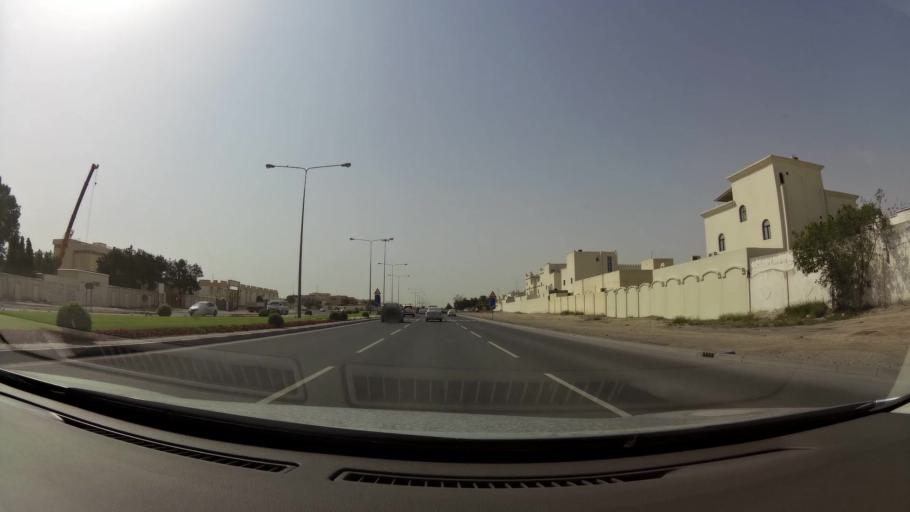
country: QA
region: Baladiyat ad Dawhah
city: Doha
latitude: 25.2478
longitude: 51.5242
